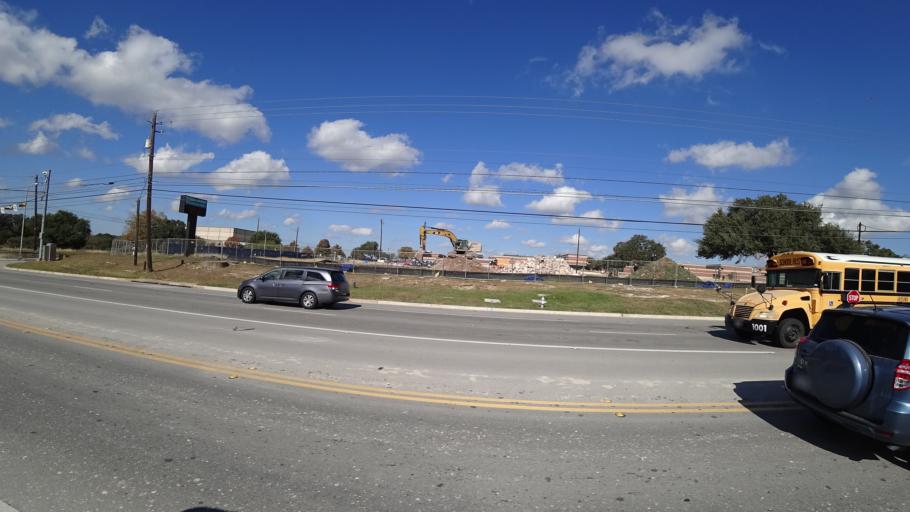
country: US
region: Texas
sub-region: Williamson County
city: Jollyville
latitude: 30.4465
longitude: -97.7337
